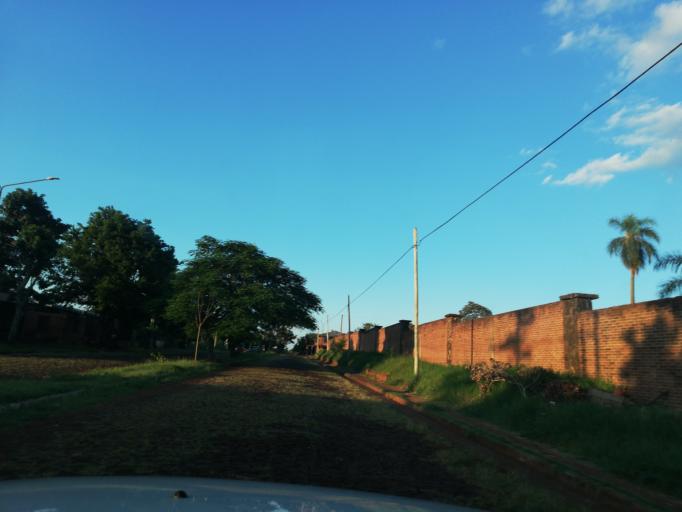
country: AR
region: Misiones
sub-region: Departamento de Capital
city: Posadas
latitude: -27.3835
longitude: -55.9491
